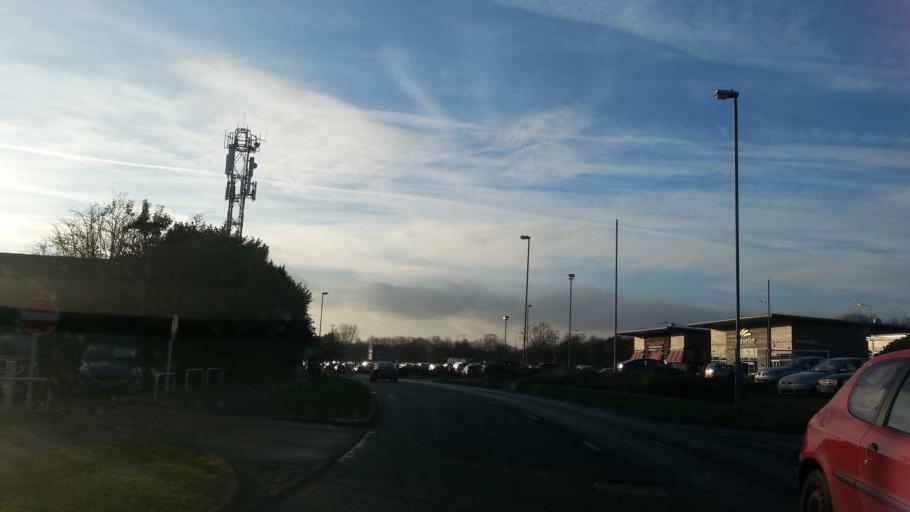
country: GB
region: England
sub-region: Northamptonshire
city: Northampton
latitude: 52.2434
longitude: -0.8361
